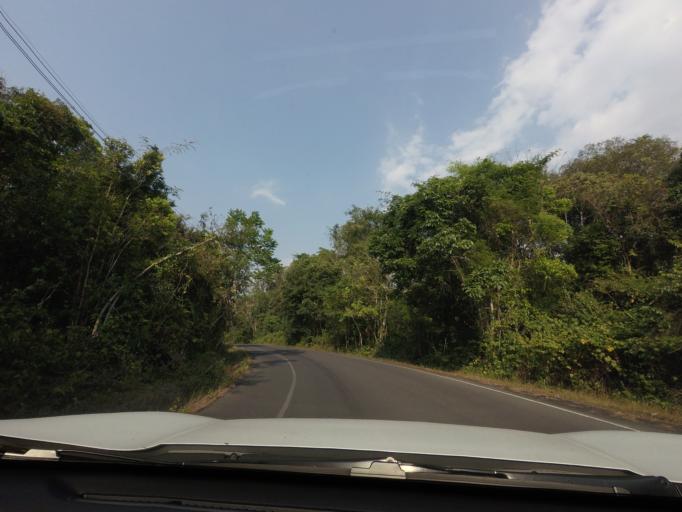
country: TH
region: Nakhon Nayok
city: Nakhon Nayok
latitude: 14.4127
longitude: 101.3776
